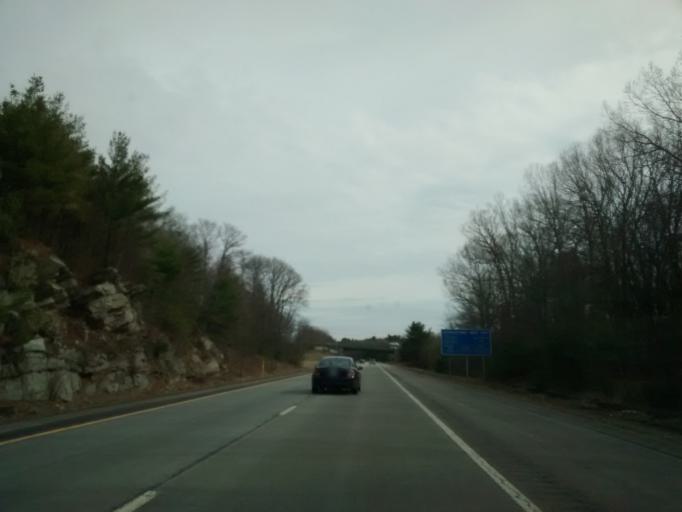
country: US
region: Massachusetts
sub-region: Worcester County
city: East Douglas
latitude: 42.0786
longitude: -71.6857
